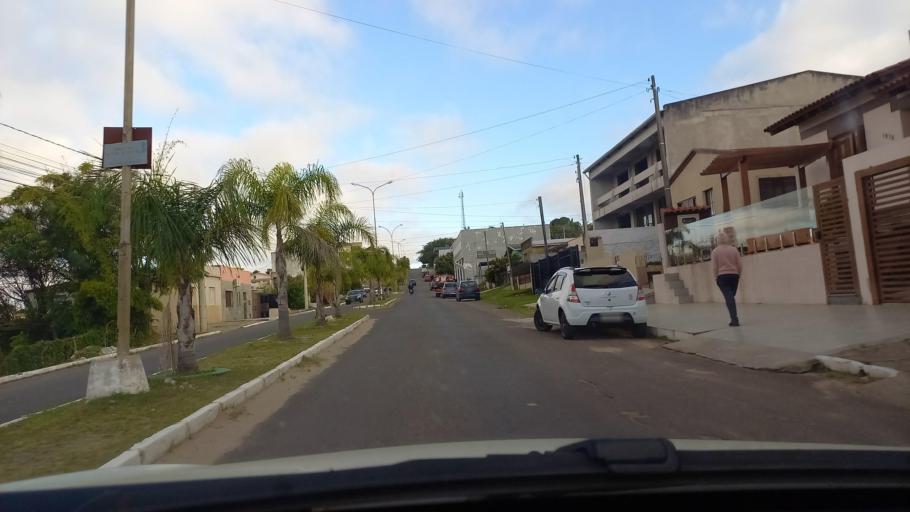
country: BR
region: Rio Grande do Sul
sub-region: Rosario Do Sul
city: Rosario do Sul
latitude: -30.2466
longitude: -54.9201
